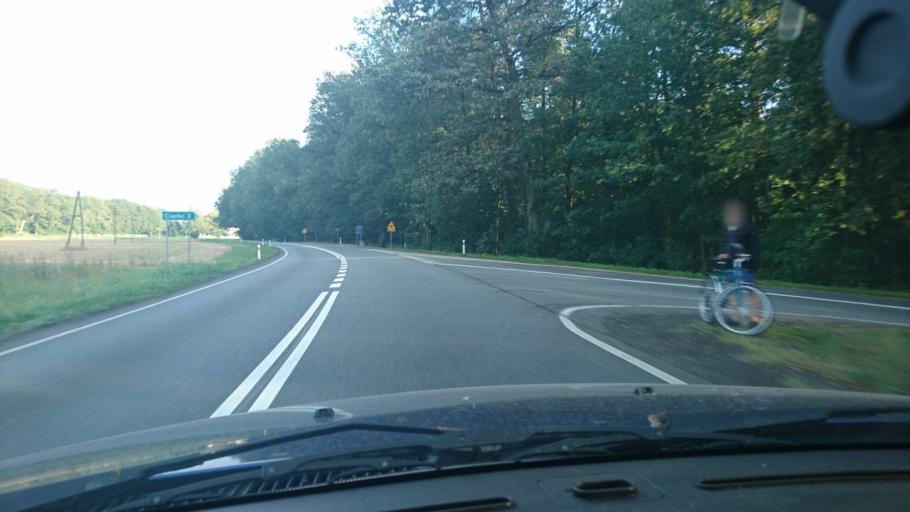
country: PL
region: Opole Voivodeship
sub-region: Powiat oleski
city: Olesno
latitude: 50.9214
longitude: 18.3390
